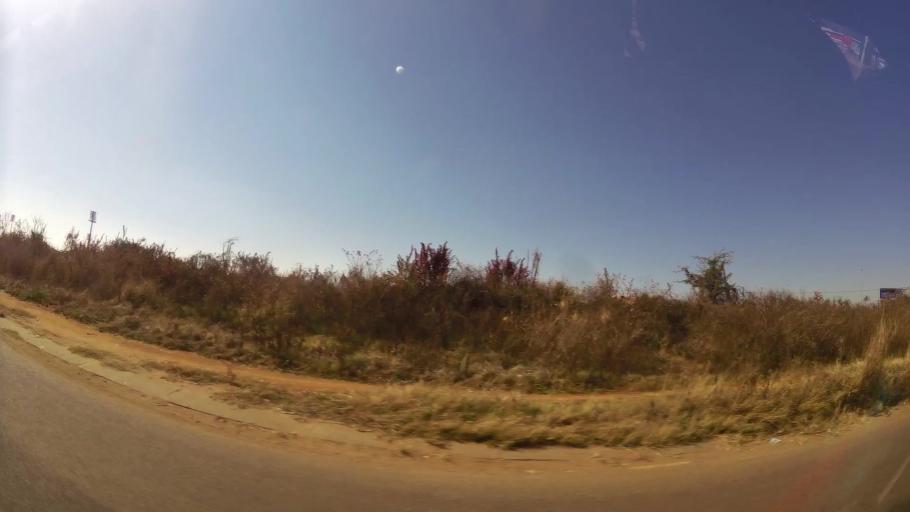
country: ZA
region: Gauteng
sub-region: City of Tshwane Metropolitan Municipality
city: Centurion
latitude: -25.8644
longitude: 28.1951
